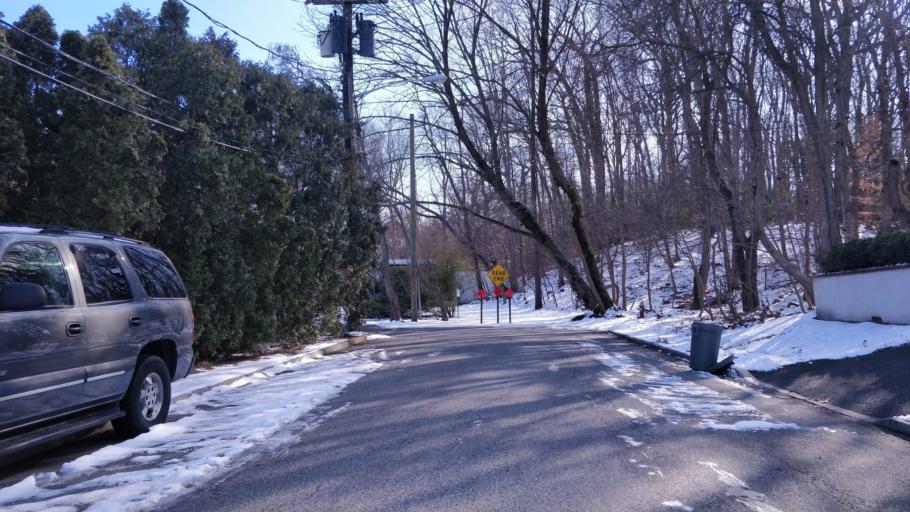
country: US
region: New York
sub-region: Nassau County
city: Oyster Bay
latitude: 40.8608
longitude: -73.5274
